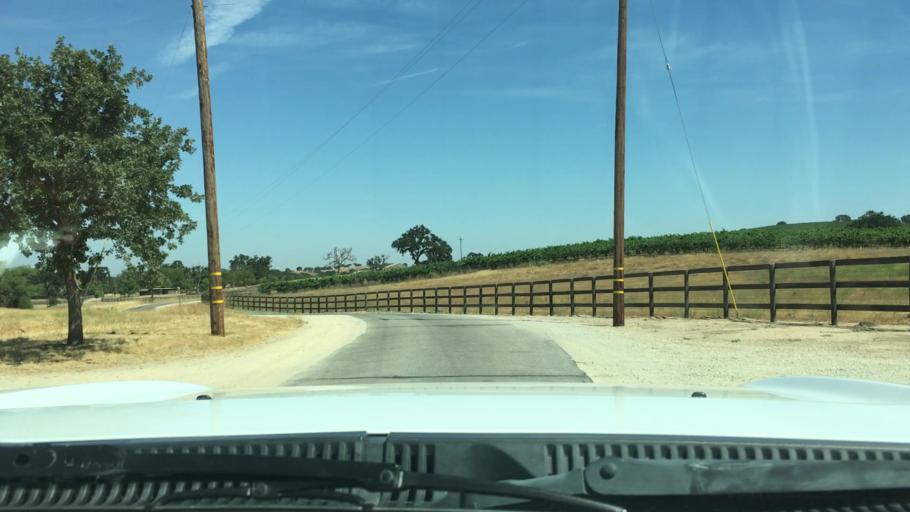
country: US
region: California
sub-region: San Luis Obispo County
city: Paso Robles
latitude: 35.5738
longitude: -120.6020
